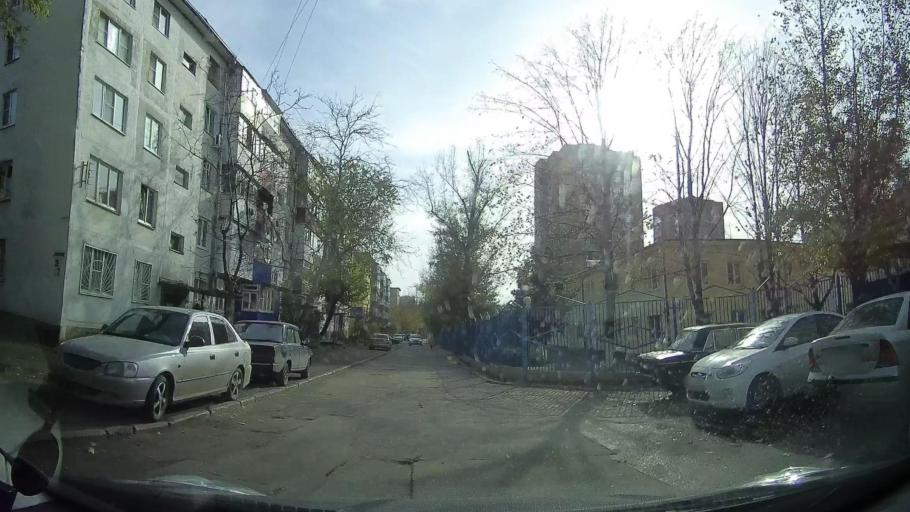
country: RU
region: Rostov
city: Severnyy
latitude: 47.2801
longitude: 39.7102
